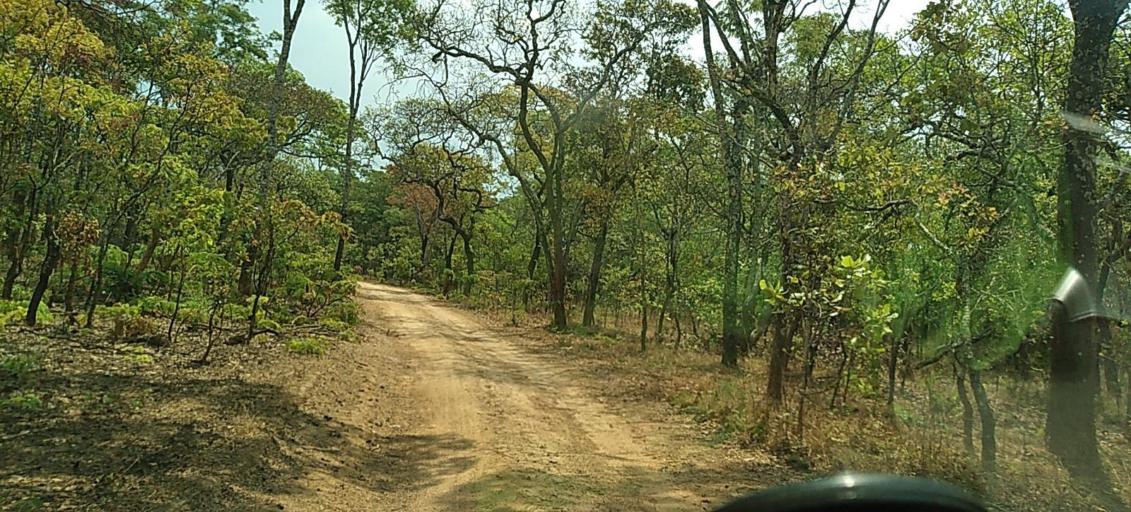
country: ZM
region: North-Western
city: Kansanshi
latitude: -12.0116
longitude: 26.2524
